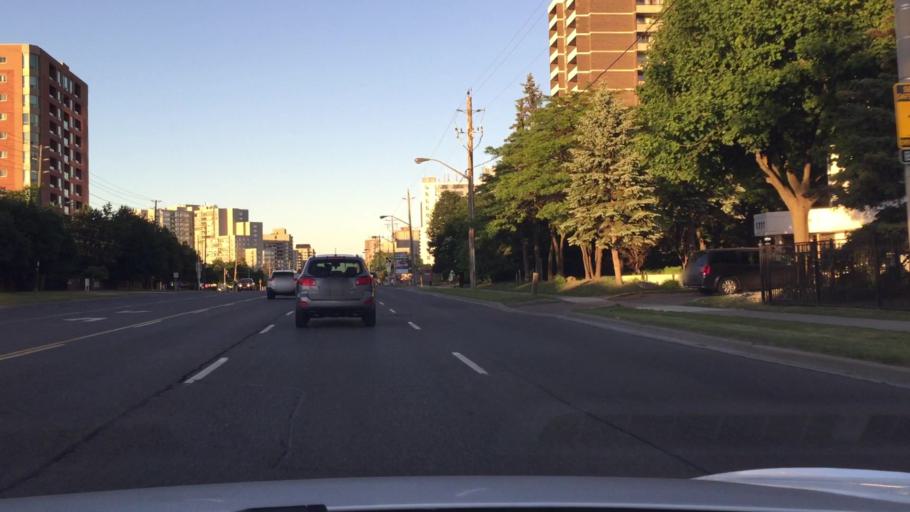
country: CA
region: Ontario
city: Concord
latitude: 43.7913
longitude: -79.4505
